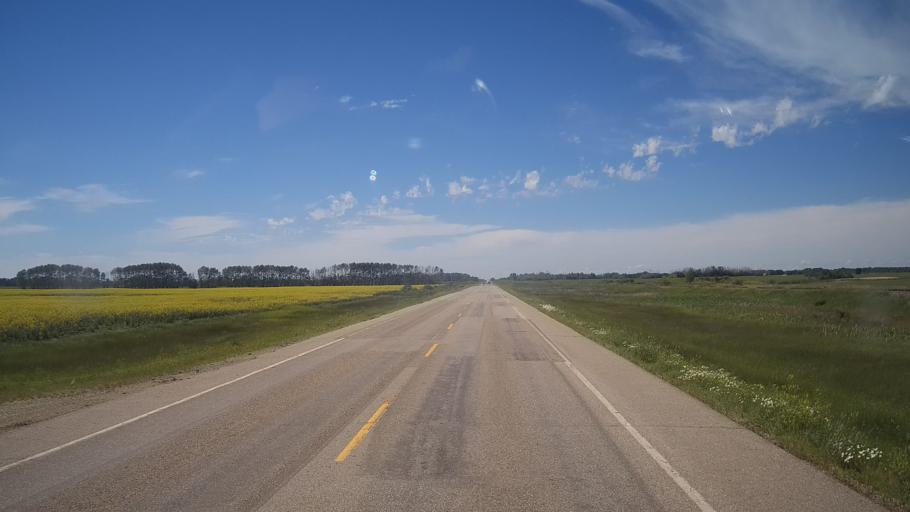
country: CA
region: Saskatchewan
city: Langenburg
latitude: 50.7879
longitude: -101.5403
